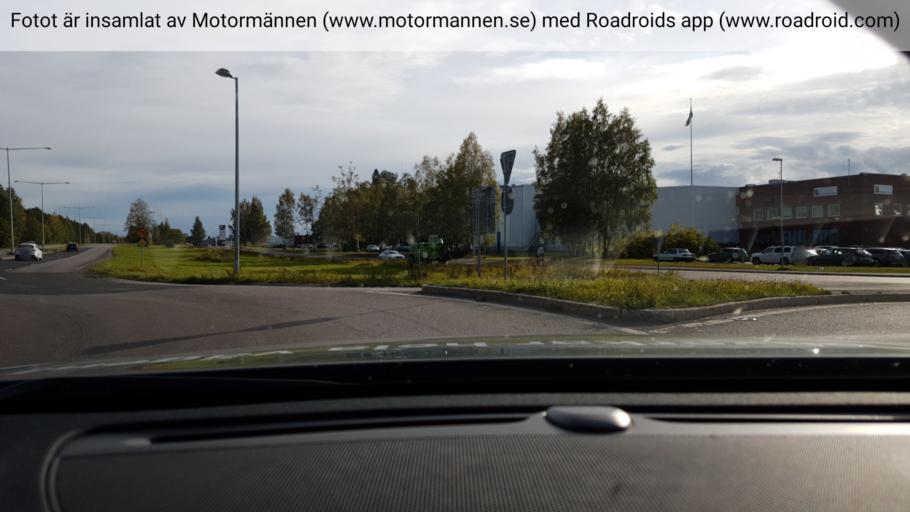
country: SE
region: Norrbotten
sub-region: Lulea Kommun
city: Lulea
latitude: 65.6130
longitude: 22.1341
